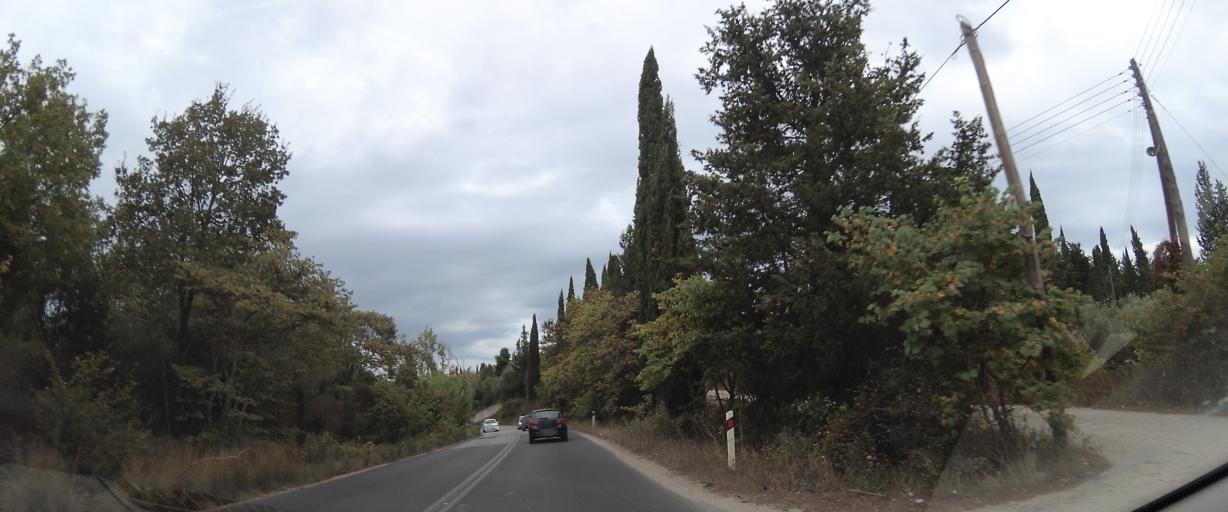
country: GR
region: Ionian Islands
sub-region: Nomos Kerkyras
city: Kontokali
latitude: 39.6967
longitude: 19.7881
